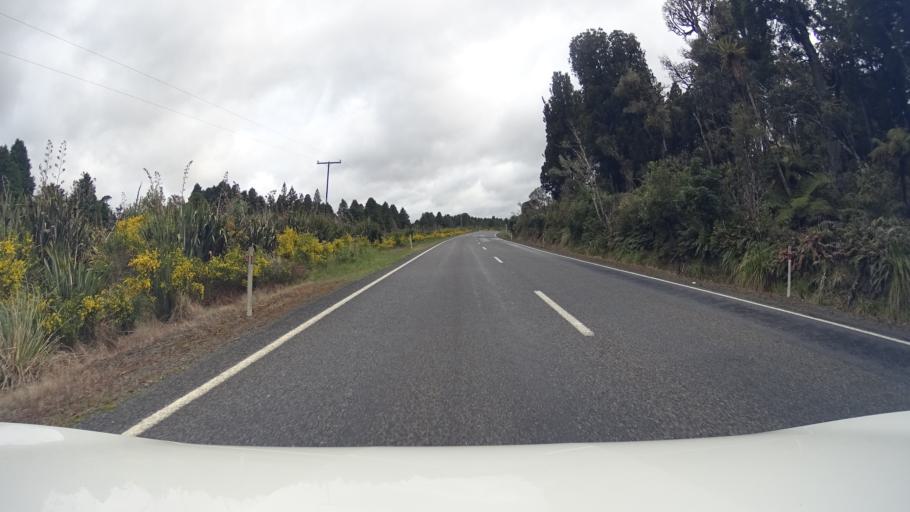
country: NZ
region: Manawatu-Wanganui
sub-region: Ruapehu District
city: Waiouru
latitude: -39.2487
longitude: 175.3887
